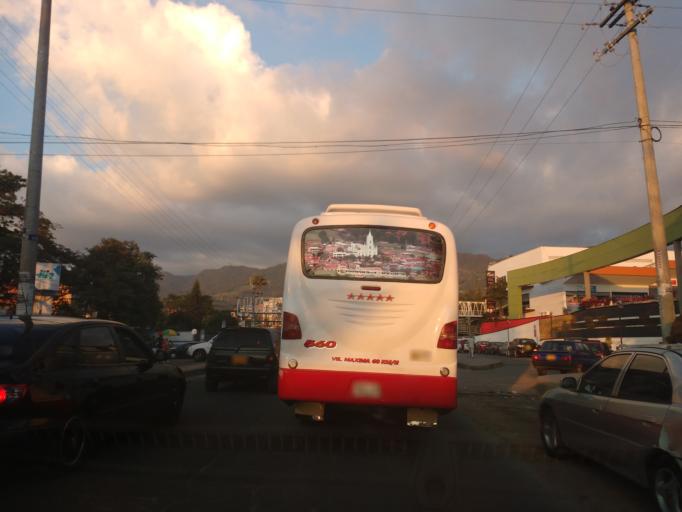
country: CO
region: Cundinamarca
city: Fusagasuga
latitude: 4.3330
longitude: -74.3710
